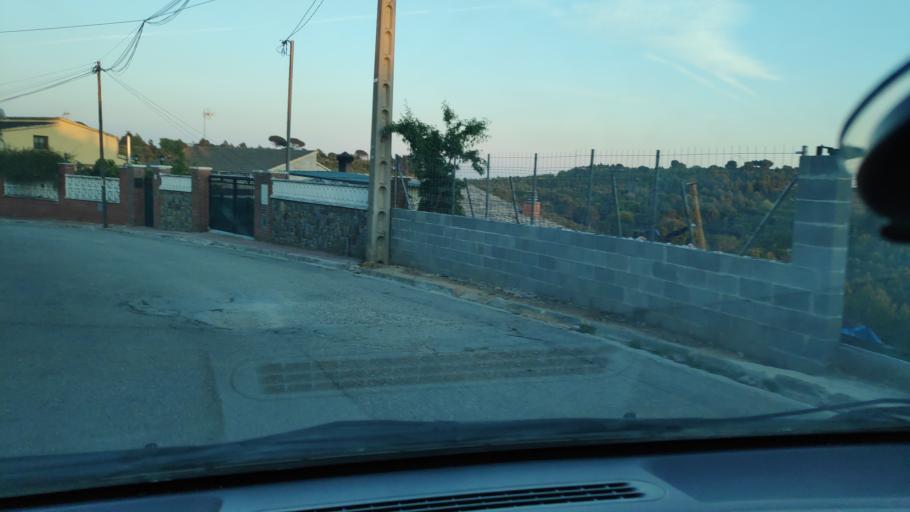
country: ES
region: Catalonia
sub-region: Provincia de Barcelona
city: Sant Quirze del Valles
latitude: 41.5301
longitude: 2.0503
